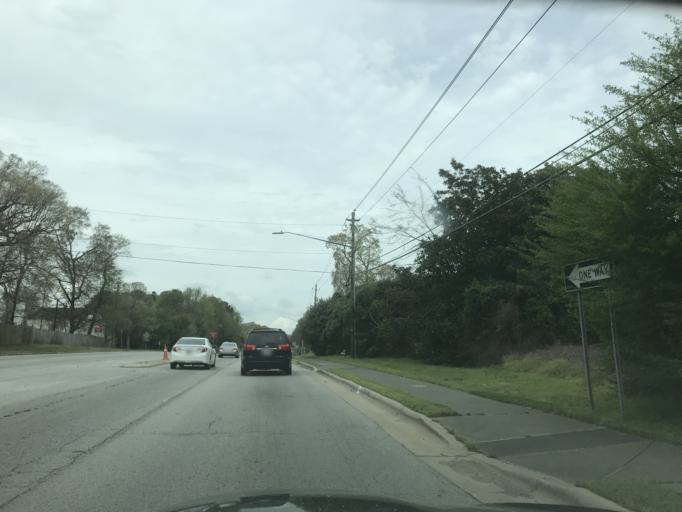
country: US
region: North Carolina
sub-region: Wake County
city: Raleigh
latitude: 35.8083
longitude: -78.5647
